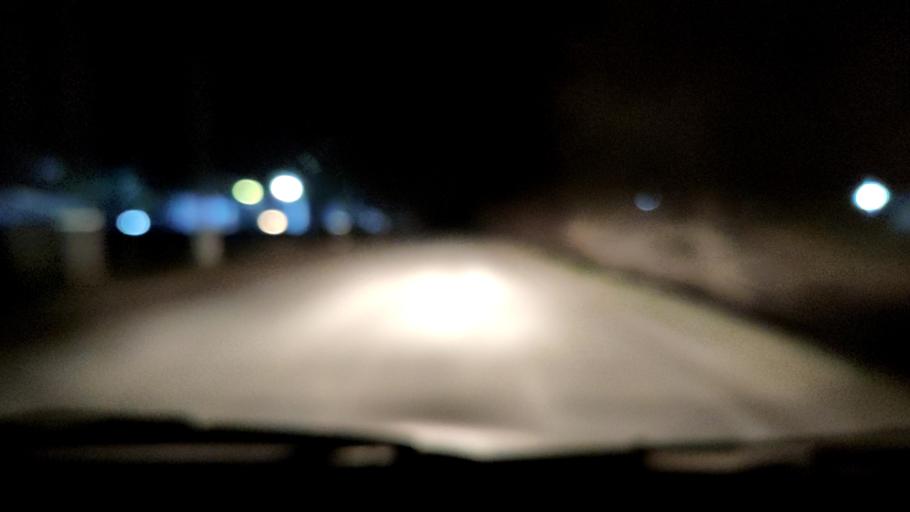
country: RU
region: Voronezj
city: Podkletnoye
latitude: 51.6426
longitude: 39.4876
